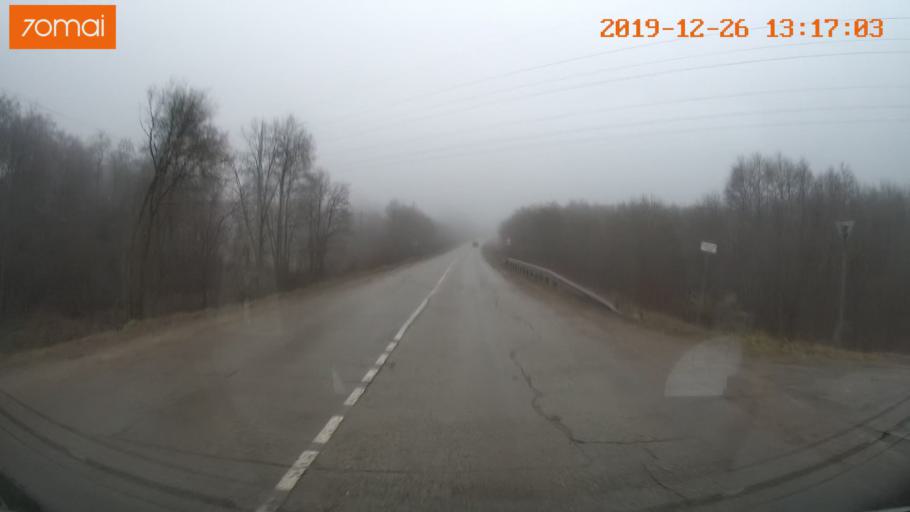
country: RU
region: Vologda
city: Cherepovets
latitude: 58.9745
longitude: 38.1117
